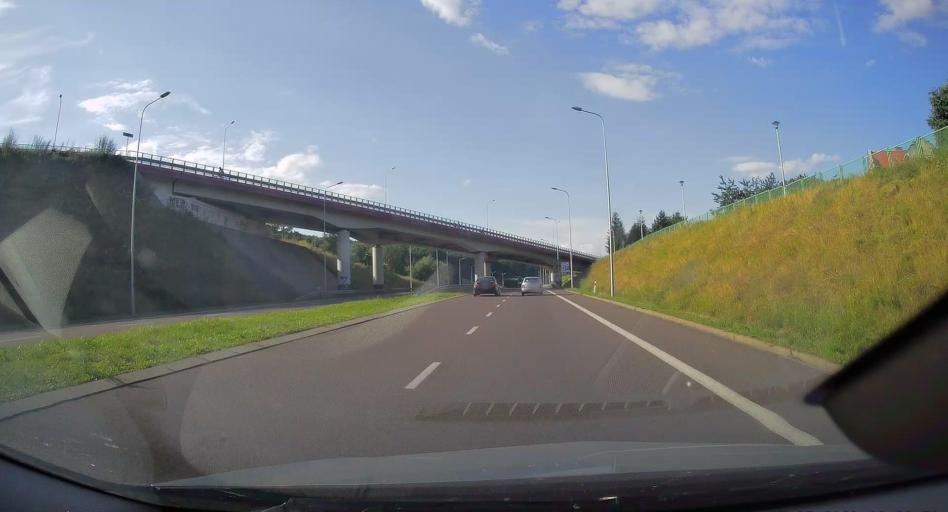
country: PL
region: Subcarpathian Voivodeship
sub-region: Powiat przemyski
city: Zurawica
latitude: 49.8058
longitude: 22.7772
